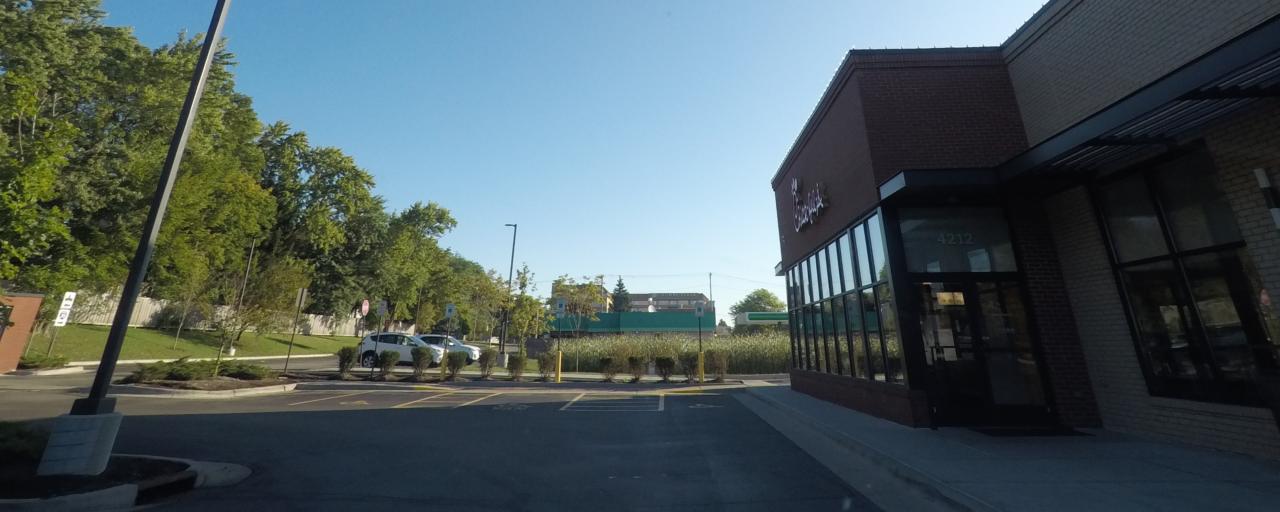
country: US
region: Wisconsin
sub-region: Dane County
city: Monona
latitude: 43.1263
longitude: -89.3118
